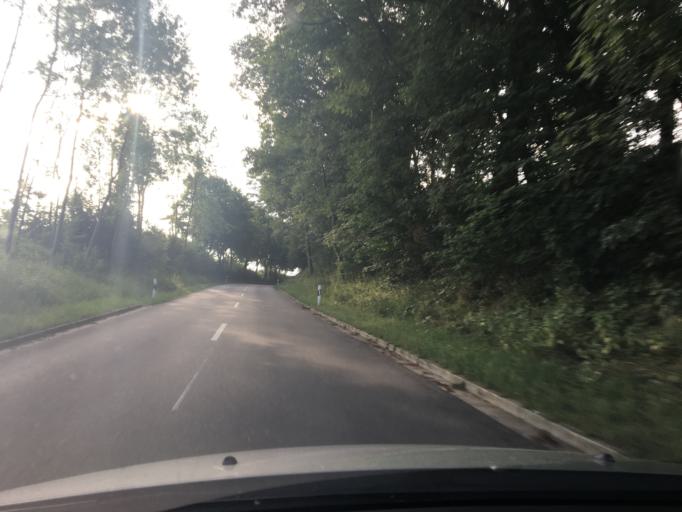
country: DE
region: Bavaria
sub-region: Lower Bavaria
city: Vilsbiburg
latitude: 48.4127
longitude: 12.3351
